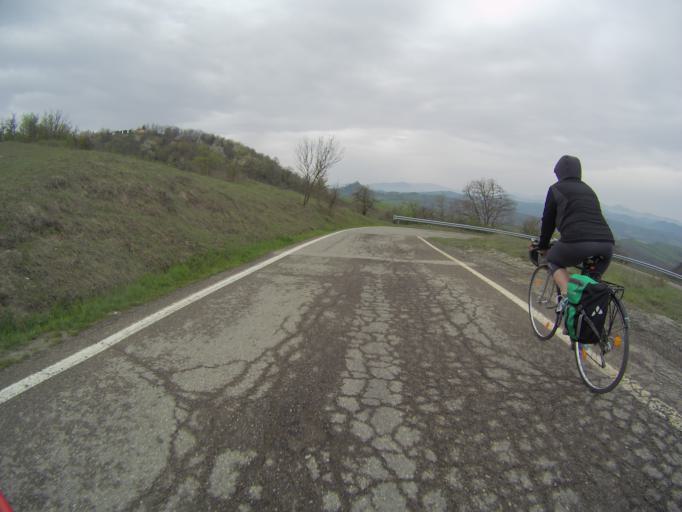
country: IT
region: Emilia-Romagna
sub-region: Provincia di Reggio Emilia
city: San Polo d'Enza
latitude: 44.5980
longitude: 10.4492
